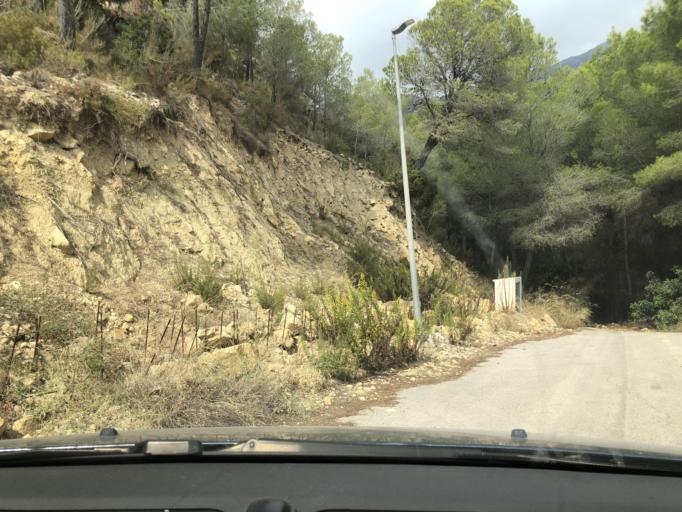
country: ES
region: Valencia
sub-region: Provincia de Alicante
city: Callosa d'En Sarria
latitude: 38.6430
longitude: -0.0703
